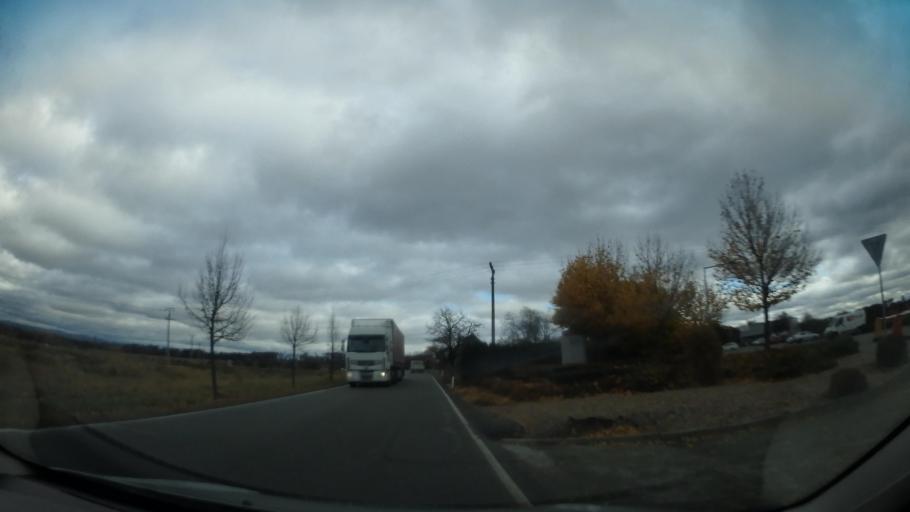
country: CZ
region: Vysocina
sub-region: Okres Zd'ar nad Sazavou
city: Velka Bites
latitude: 49.2704
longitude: 16.2350
